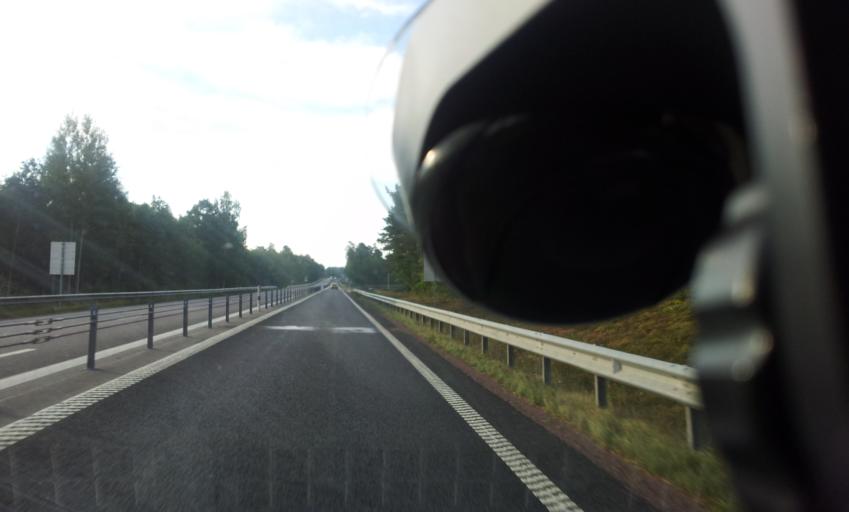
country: SE
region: Kalmar
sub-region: Kalmar Kommun
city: Lindsdal
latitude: 56.8267
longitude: 16.3677
